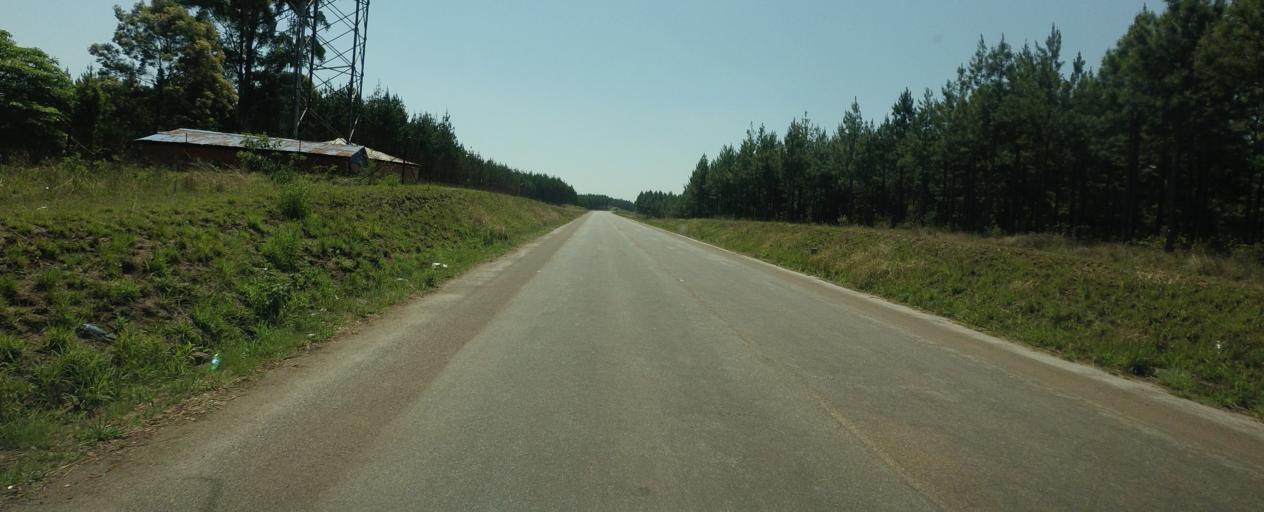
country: ZA
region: Mpumalanga
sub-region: Ehlanzeni District
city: Graksop
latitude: -24.9036
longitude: 30.8449
